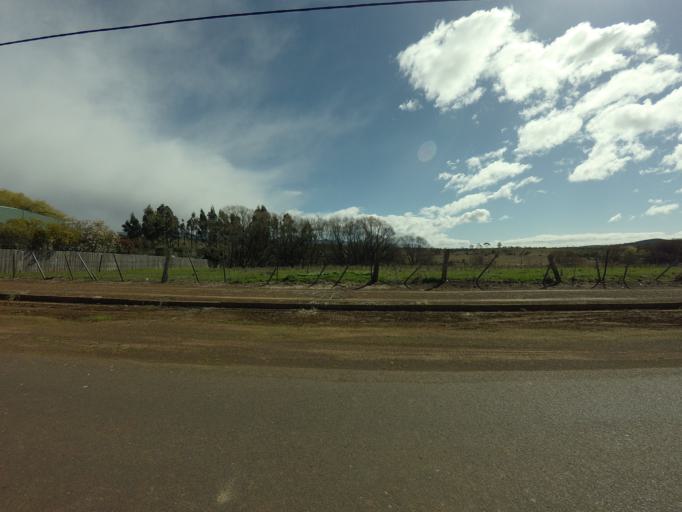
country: AU
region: Tasmania
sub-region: Northern Midlands
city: Evandale
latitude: -42.1383
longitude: 147.4257
